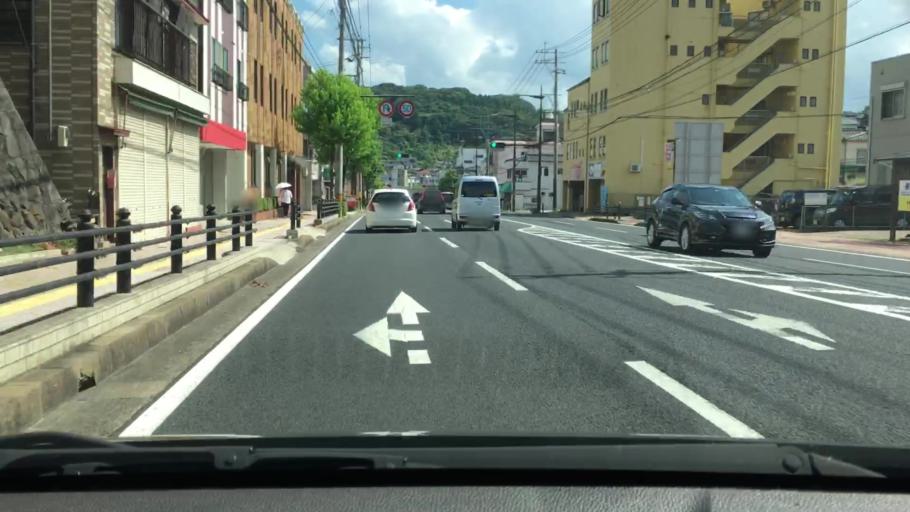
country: JP
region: Nagasaki
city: Sasebo
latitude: 33.2004
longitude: 129.7215
